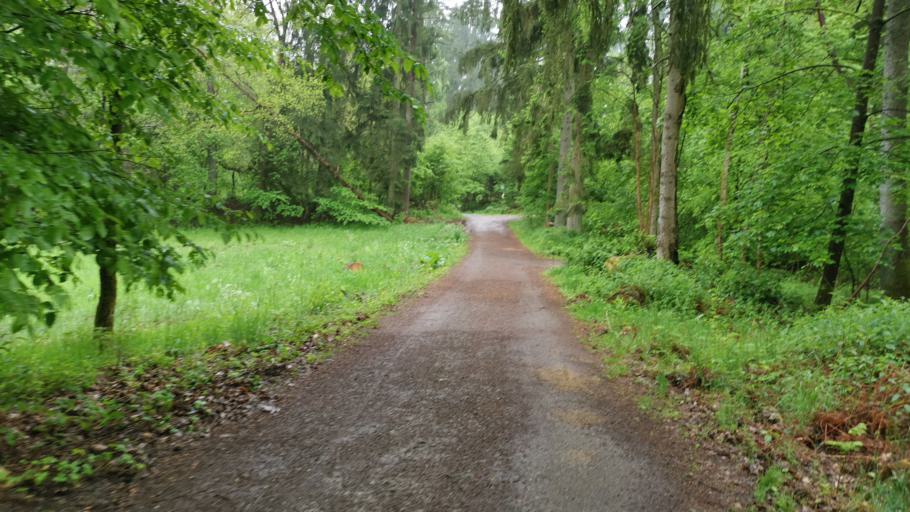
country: DE
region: Saarland
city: Kirkel
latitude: 49.2621
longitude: 7.1868
